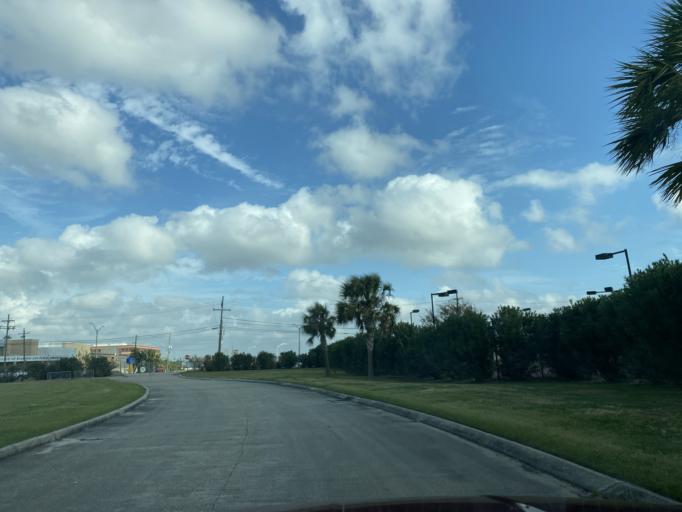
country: US
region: Louisiana
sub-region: Orleans Parish
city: New Orleans
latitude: 30.0292
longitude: -90.0472
